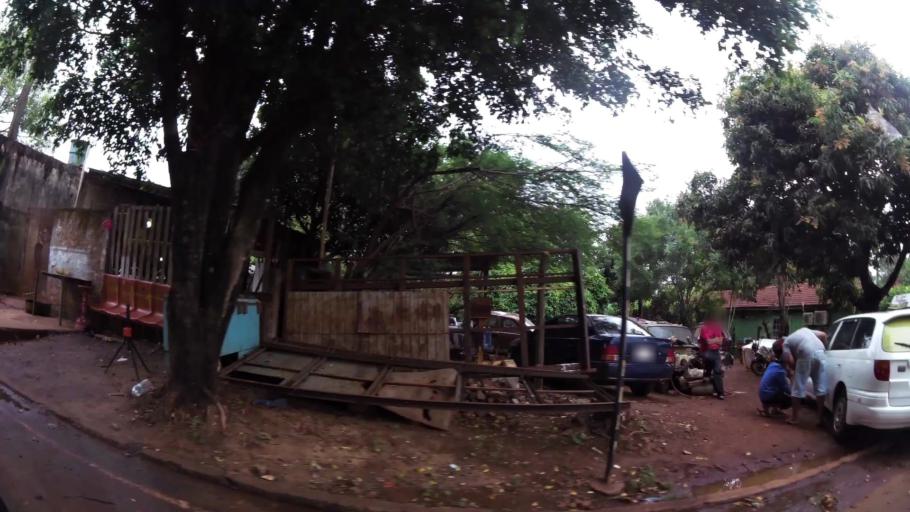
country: PY
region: Alto Parana
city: Ciudad del Este
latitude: -25.4816
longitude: -54.7674
